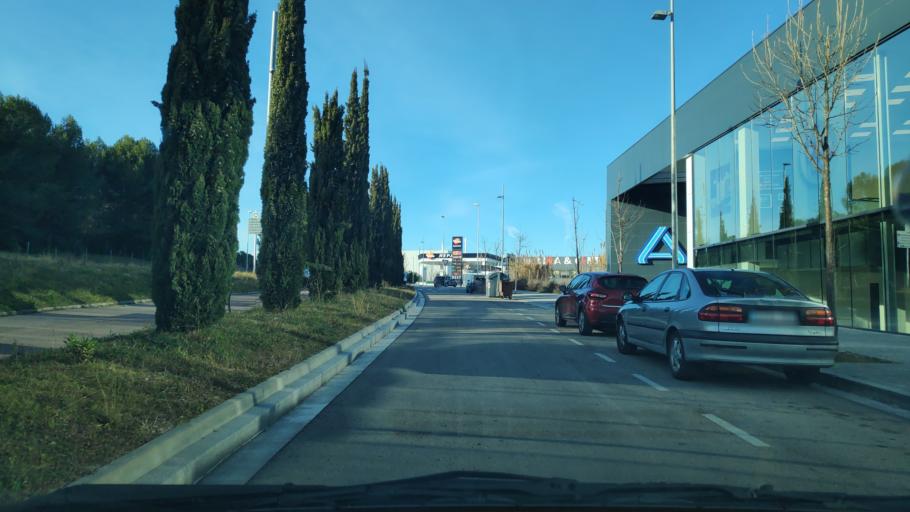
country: ES
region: Catalonia
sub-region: Provincia de Barcelona
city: Mollet del Valles
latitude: 41.5347
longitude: 2.2045
